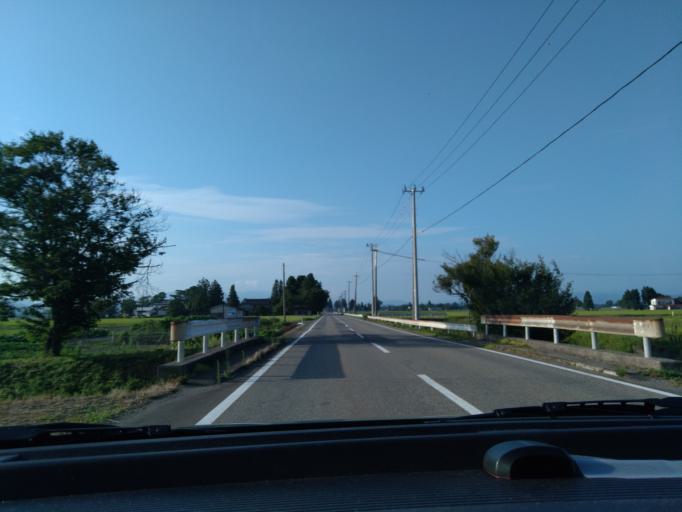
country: JP
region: Akita
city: Kakunodatemachi
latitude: 39.5213
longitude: 140.5583
